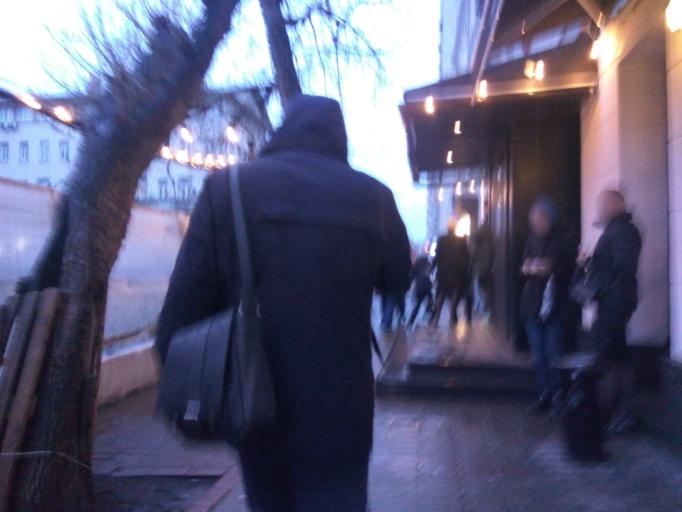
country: RU
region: Moscow
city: Moscow
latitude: 55.7713
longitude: 37.5953
